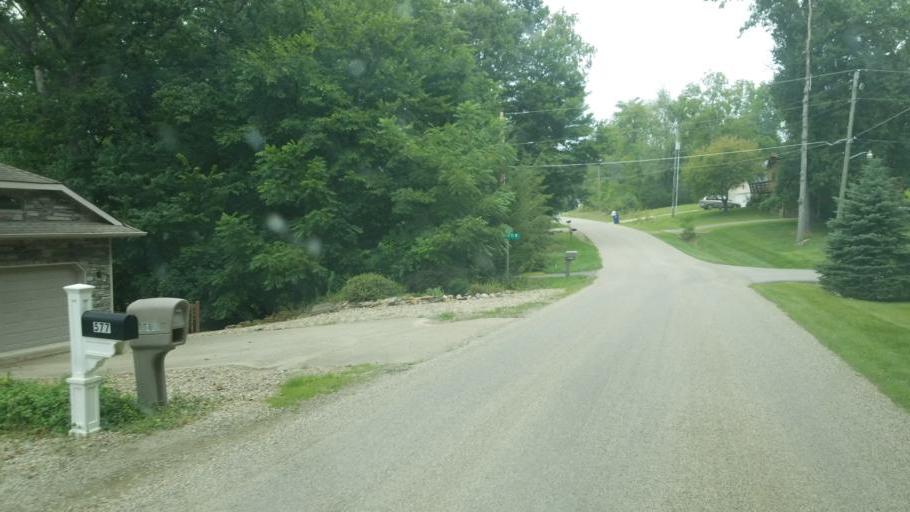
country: US
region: Ohio
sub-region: Knox County
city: Danville
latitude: 40.4514
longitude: -82.3368
